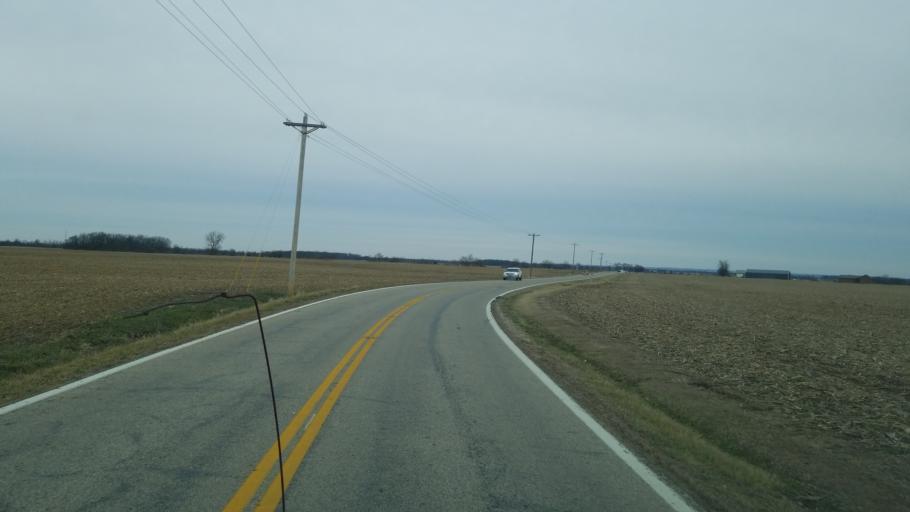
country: US
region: Ohio
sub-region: Pickaway County
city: Williamsport
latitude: 39.5544
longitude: -83.1022
